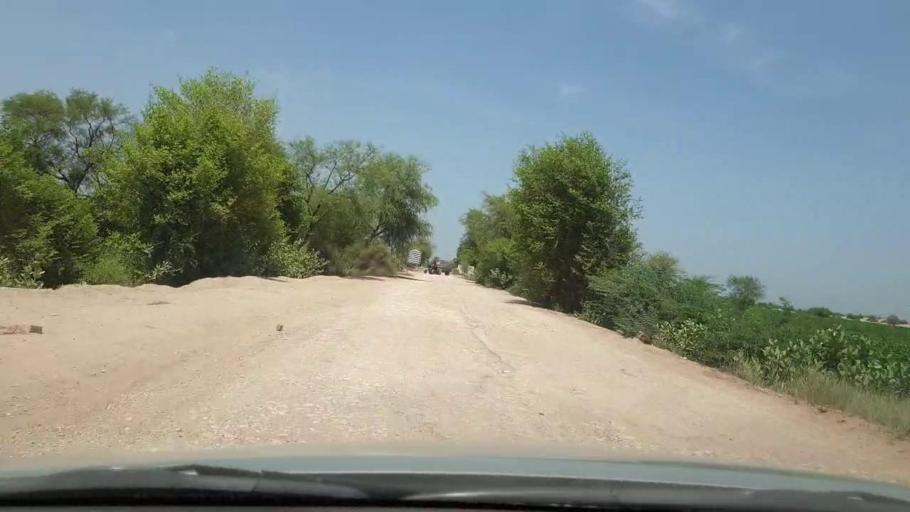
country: PK
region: Sindh
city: Pano Aqil
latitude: 27.7007
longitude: 69.2178
